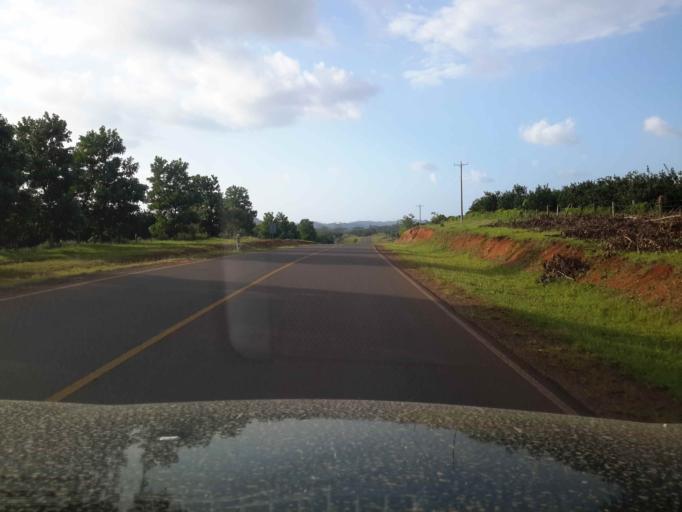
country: NI
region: Rio San Juan
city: San Carlos
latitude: 11.1616
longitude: -84.6611
